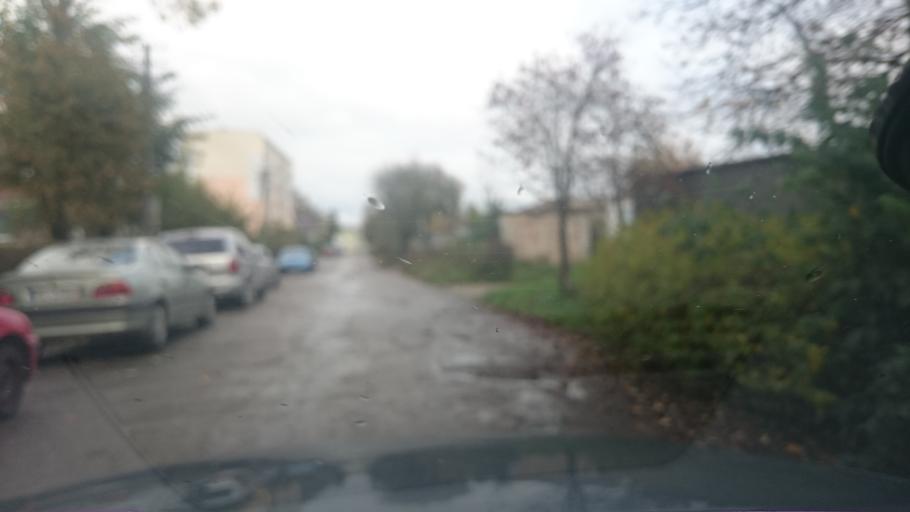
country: PL
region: Pomeranian Voivodeship
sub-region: Sopot
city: Sopot
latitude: 54.3978
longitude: 18.5823
